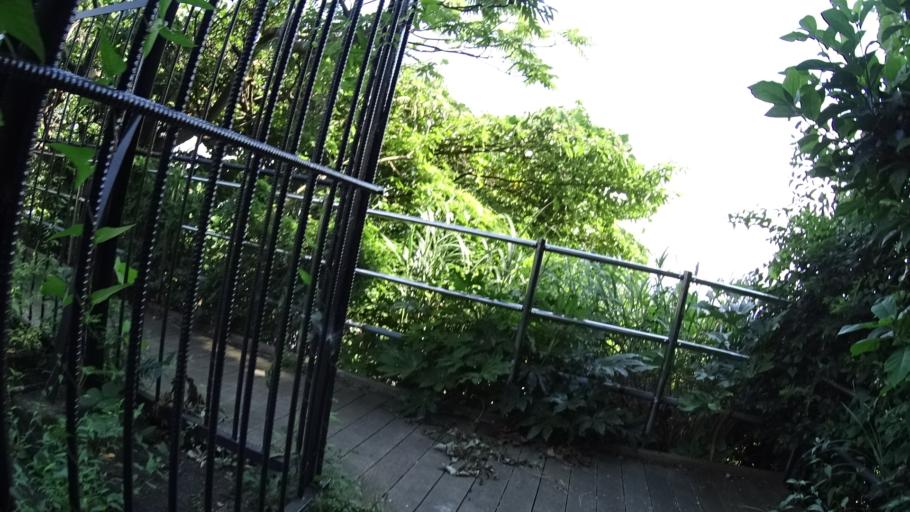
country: JP
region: Kanagawa
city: Zushi
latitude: 35.3074
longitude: 139.6163
